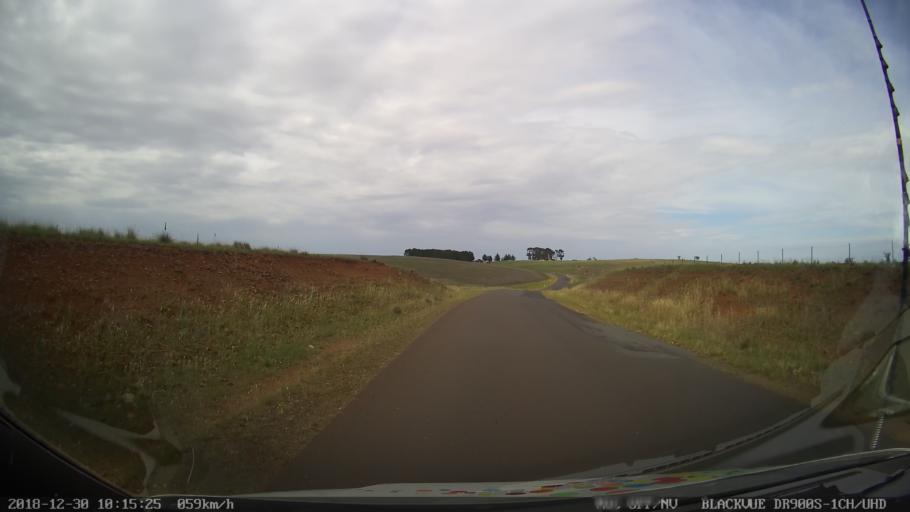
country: AU
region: New South Wales
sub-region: Snowy River
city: Berridale
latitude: -36.5430
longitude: 149.0461
